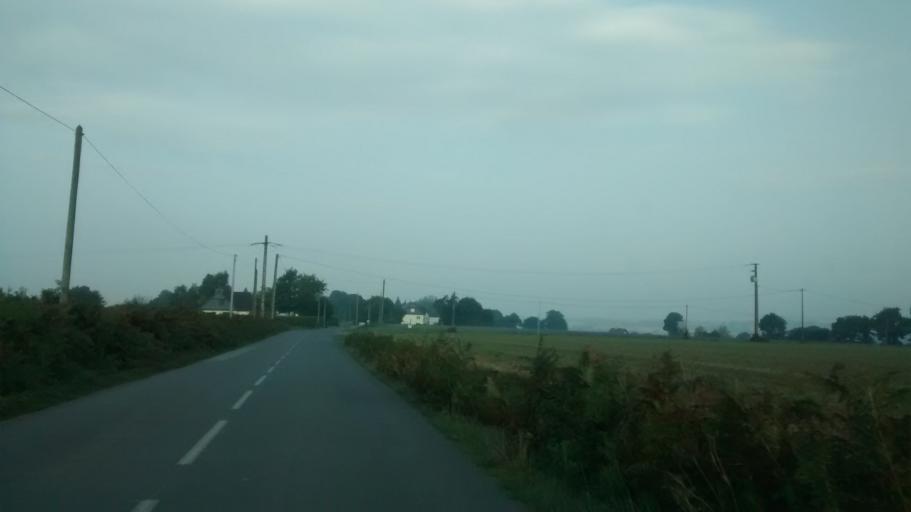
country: FR
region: Brittany
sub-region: Departement d'Ille-et-Vilaine
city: Poce-les-Bois
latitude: 48.1347
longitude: -1.2529
